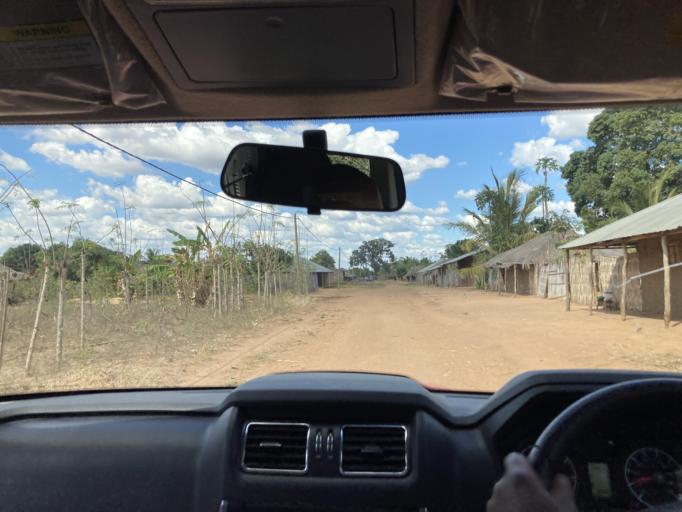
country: MZ
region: Cabo Delgado
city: Montepuez
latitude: -13.1466
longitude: 38.9978
